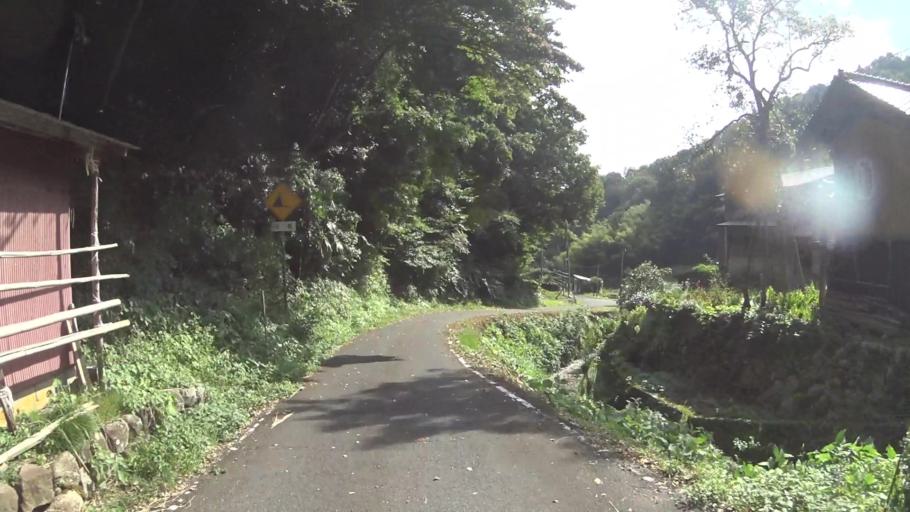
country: JP
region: Kyoto
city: Miyazu
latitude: 35.6111
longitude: 135.1972
